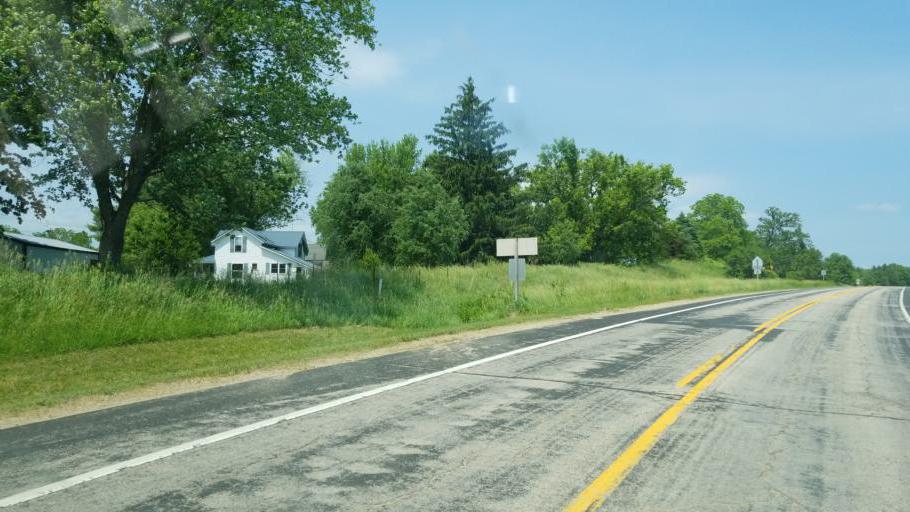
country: US
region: Wisconsin
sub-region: Monroe County
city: Cashton
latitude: 43.5811
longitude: -90.6408
